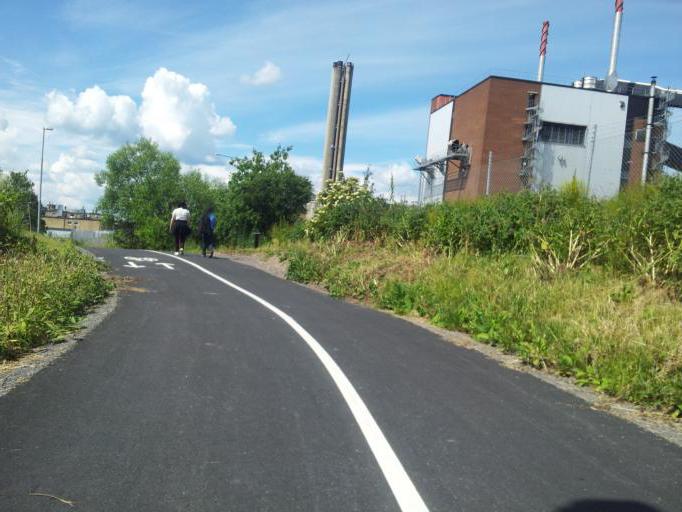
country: SE
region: Uppsala
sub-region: Uppsala Kommun
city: Saevja
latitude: 59.8506
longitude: 17.6809
